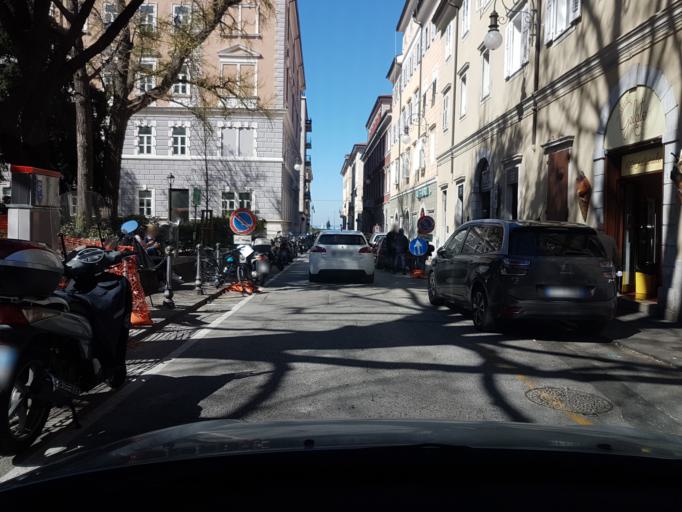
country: IT
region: Friuli Venezia Giulia
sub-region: Provincia di Trieste
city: Trieste
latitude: 45.6472
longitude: 13.7656
